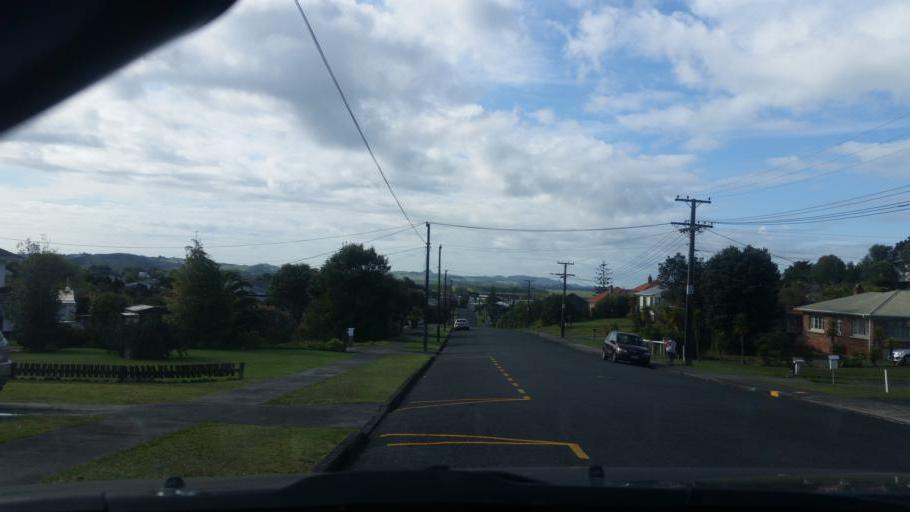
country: NZ
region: Northland
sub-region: Kaipara District
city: Dargaville
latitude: -35.9333
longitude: 173.8676
